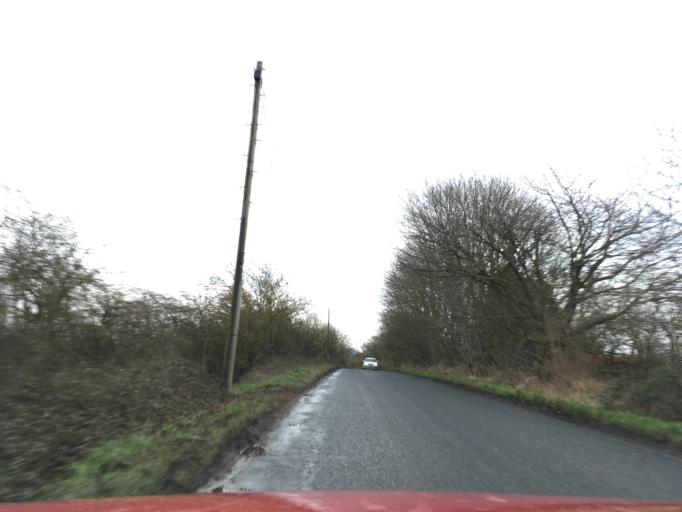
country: GB
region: England
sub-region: Worcestershire
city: Evesham
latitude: 52.0381
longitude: -1.9952
